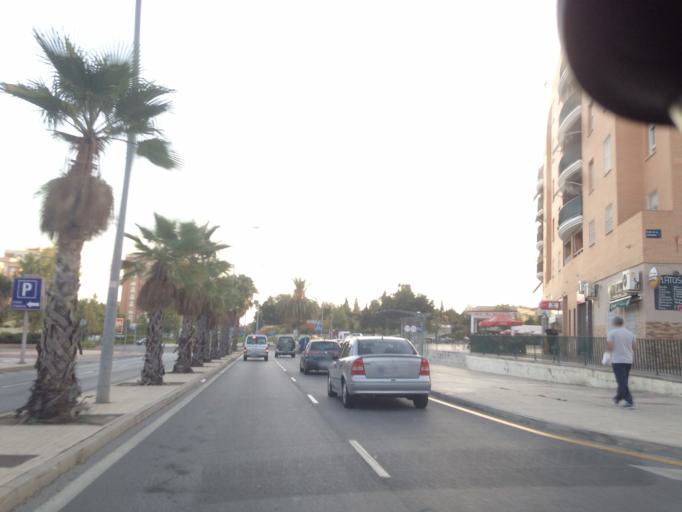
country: ES
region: Andalusia
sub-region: Provincia de Malaga
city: Malaga
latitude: 36.7347
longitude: -4.4335
